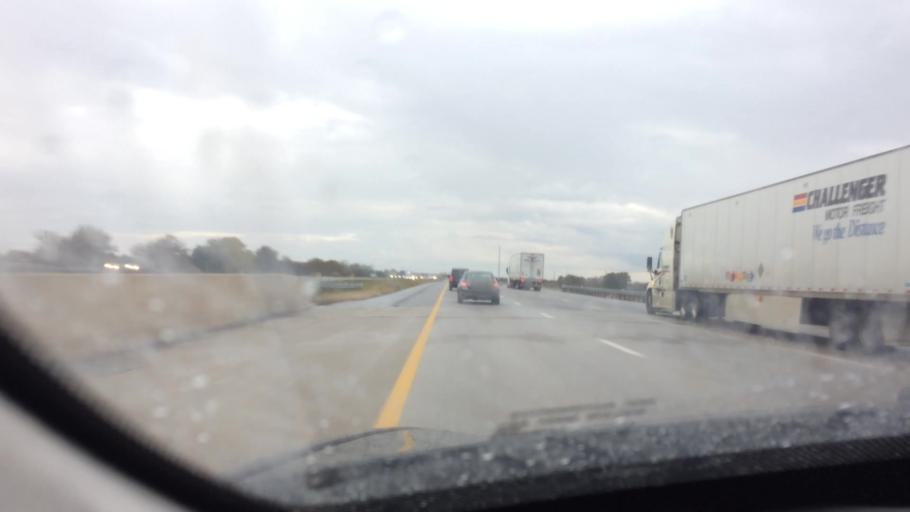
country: US
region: Ohio
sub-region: Wood County
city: Bowling Green
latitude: 41.4172
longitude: -83.6156
